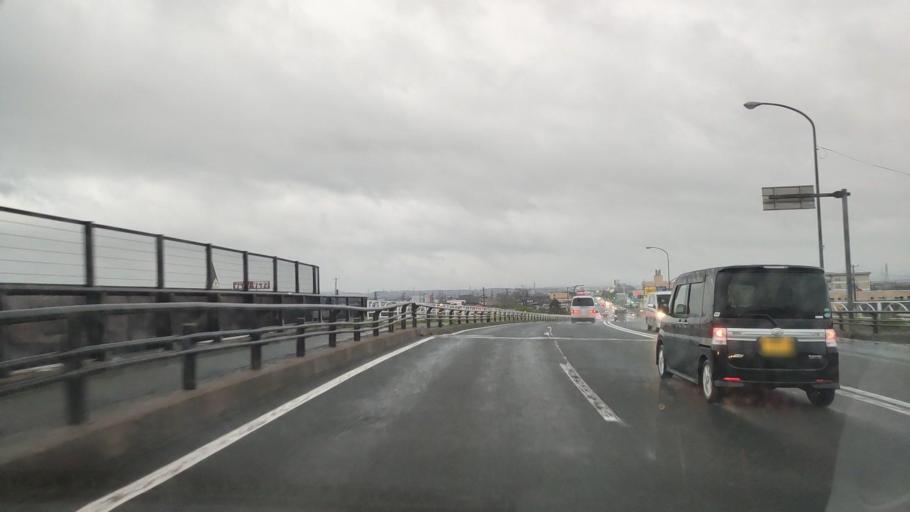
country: JP
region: Akita
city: Akita
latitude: 39.6972
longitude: 140.1184
